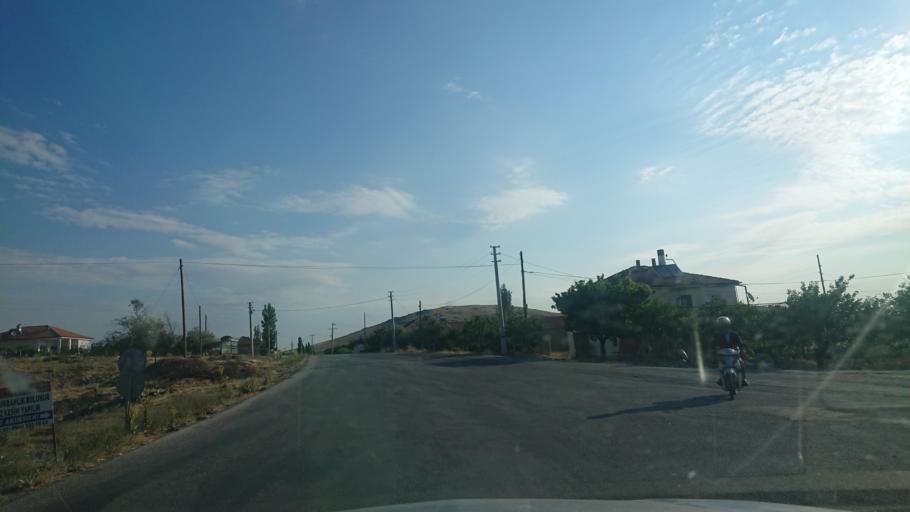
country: TR
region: Aksaray
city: Ortakoy
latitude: 38.7618
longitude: 34.0611
